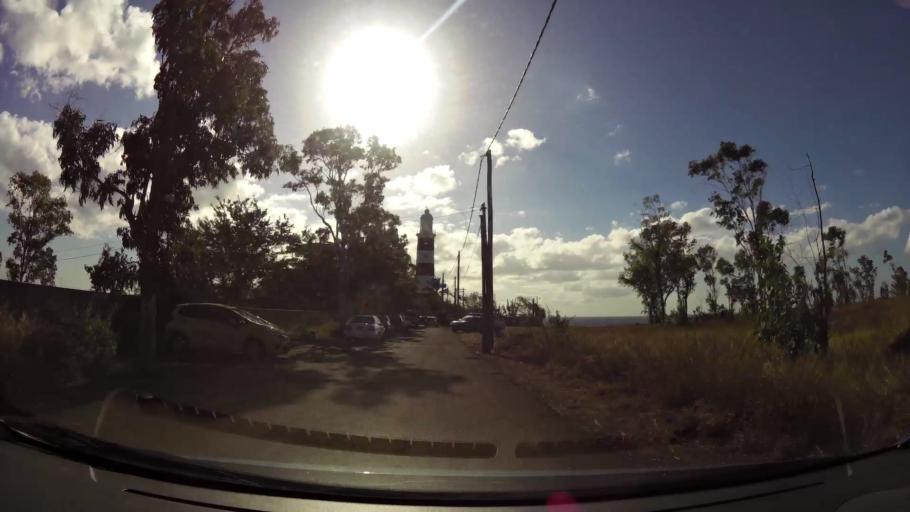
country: MU
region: Black River
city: Albion
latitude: -20.1921
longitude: 57.4123
